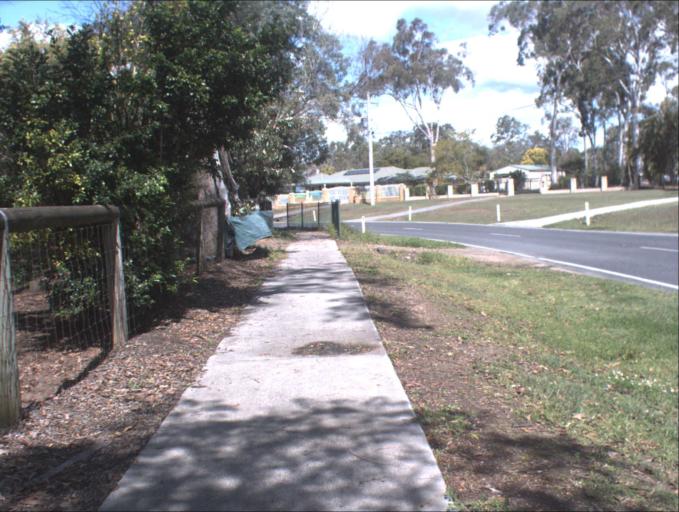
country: AU
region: Queensland
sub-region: Logan
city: Park Ridge South
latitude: -27.7406
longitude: 153.0346
